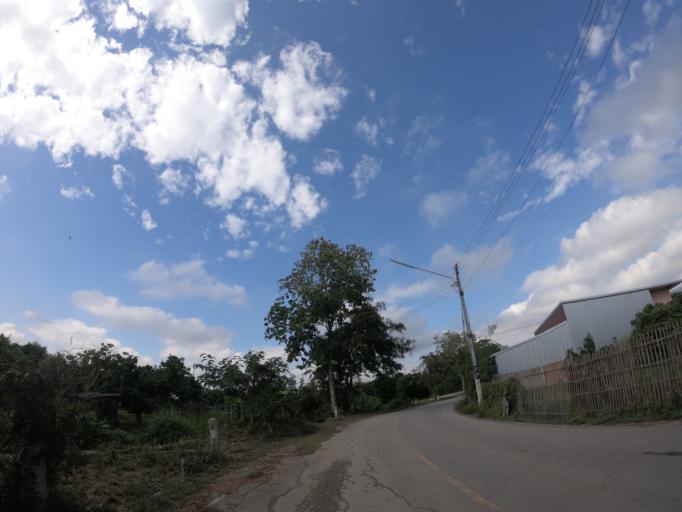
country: TH
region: Chiang Mai
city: Saraphi
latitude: 18.7042
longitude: 98.9766
